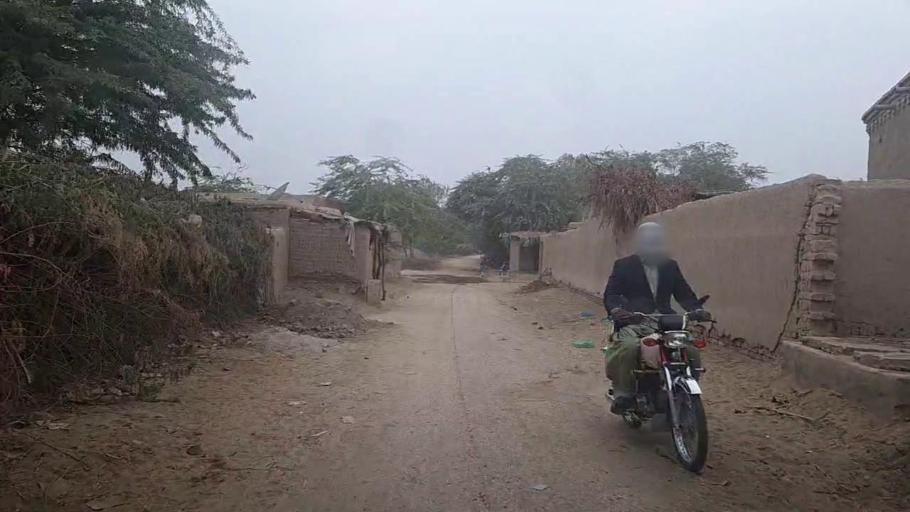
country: PK
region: Sindh
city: Gambat
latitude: 27.3499
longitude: 68.6009
